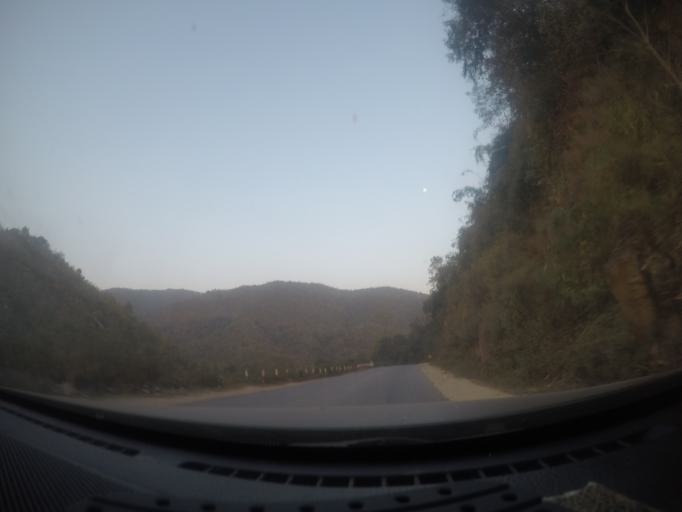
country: MM
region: Mandalay
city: Yamethin
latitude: 20.8157
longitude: 96.4429
